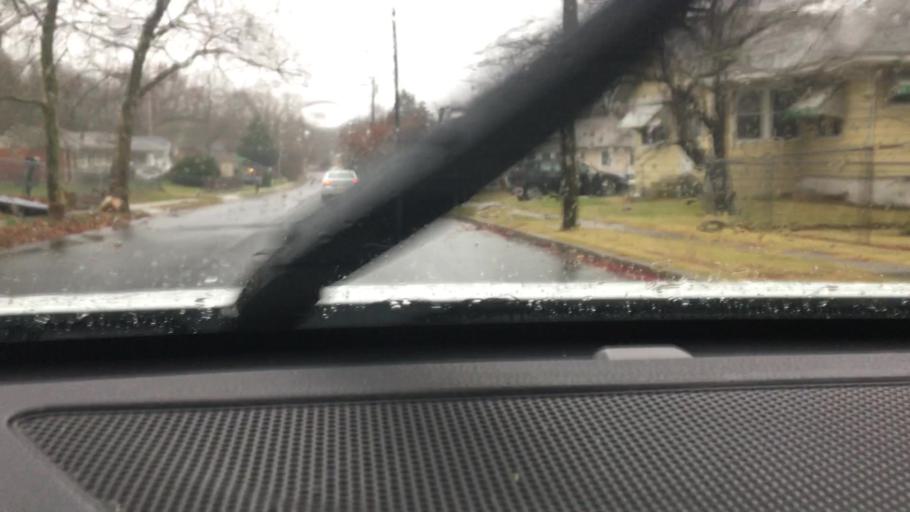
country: US
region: New Jersey
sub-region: Atlantic County
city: Pleasantville
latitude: 39.4027
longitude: -74.5293
